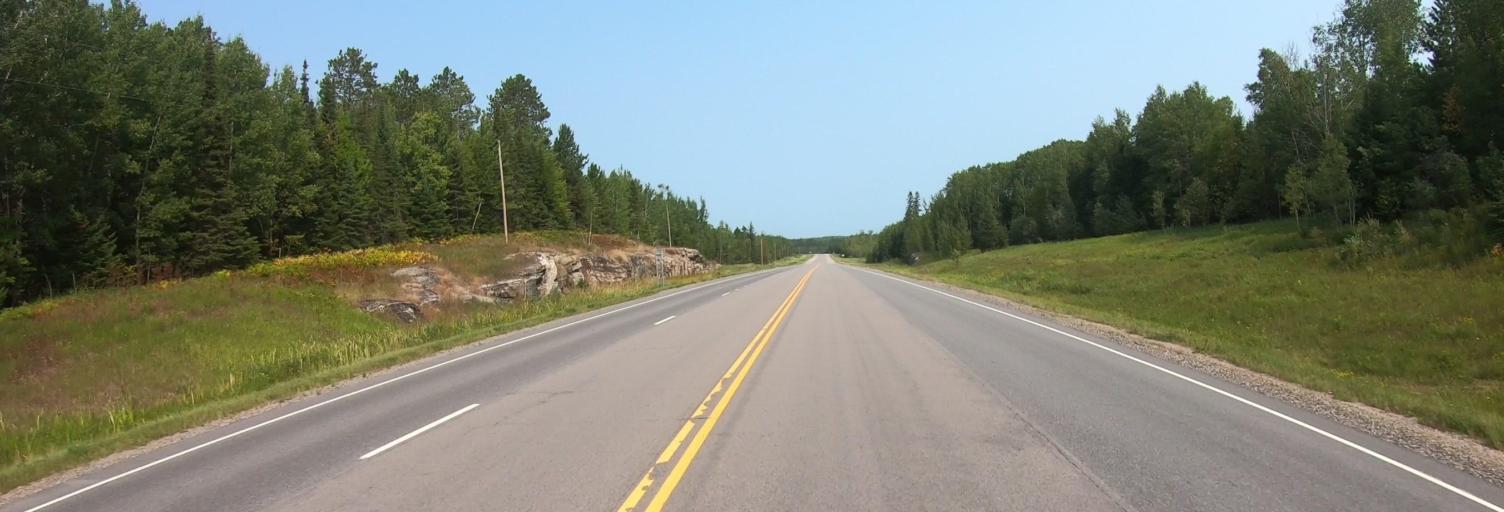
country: US
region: Minnesota
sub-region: Saint Louis County
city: Mountain Iron
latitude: 48.0761
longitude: -92.8224
